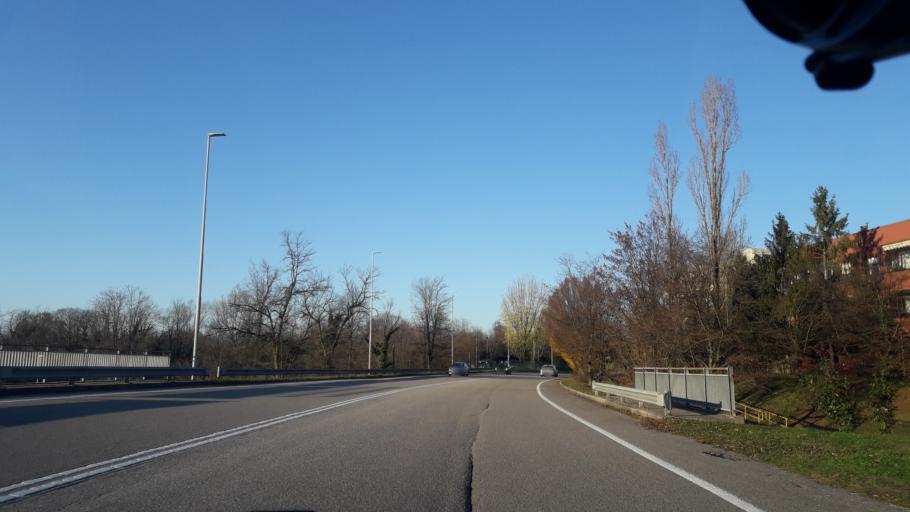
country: IT
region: Friuli Venezia Giulia
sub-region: Provincia di Udine
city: Passons
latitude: 46.0708
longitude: 13.2037
